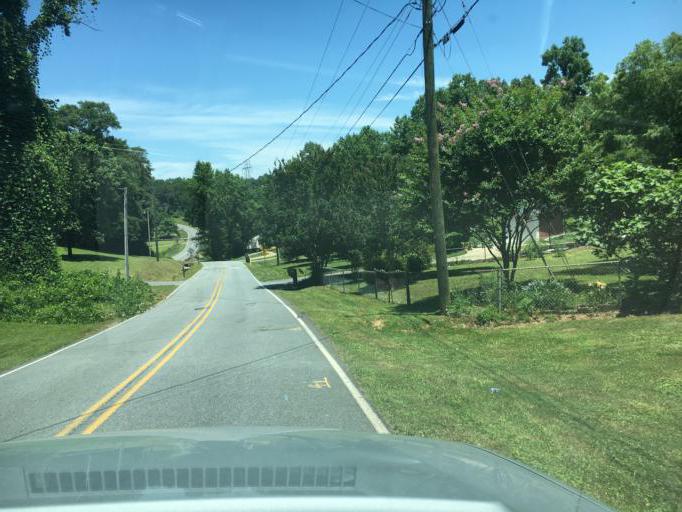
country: US
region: South Carolina
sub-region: Greenville County
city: Greer
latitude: 34.9561
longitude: -82.2241
